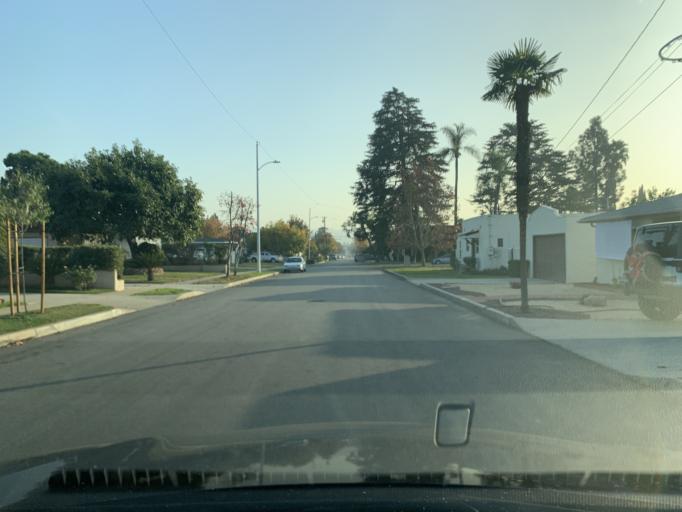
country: US
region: California
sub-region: Los Angeles County
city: Covina
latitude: 34.0881
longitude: -117.8836
